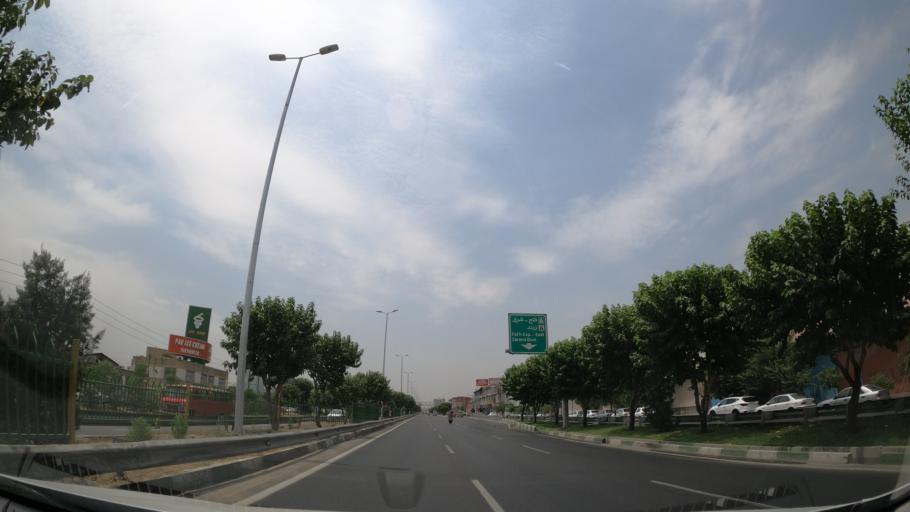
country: IR
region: Tehran
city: Tehran
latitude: 35.6751
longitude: 51.3200
